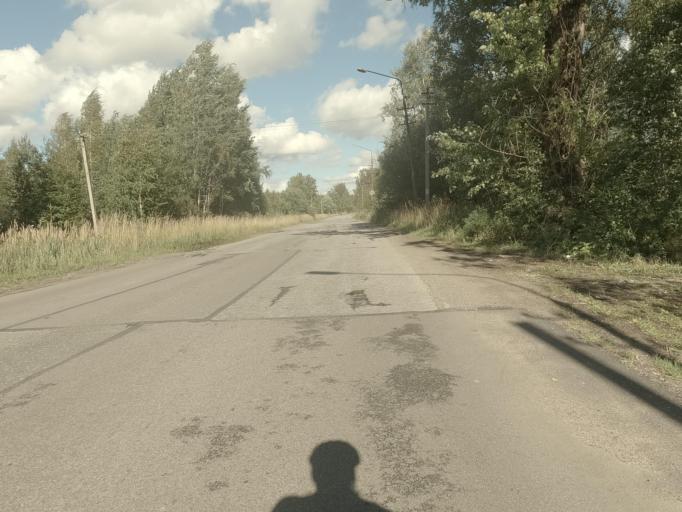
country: RU
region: Leningrad
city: Yanino Vtoroye
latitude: 59.9815
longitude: 30.5810
